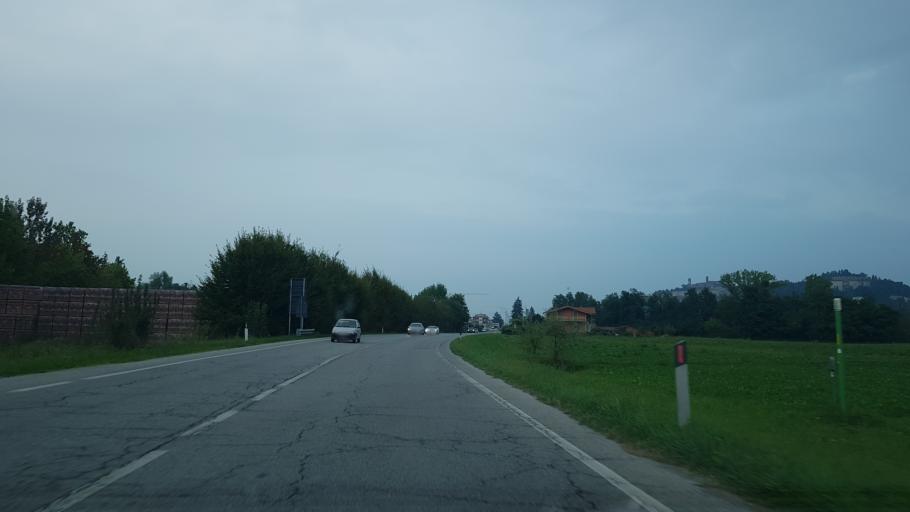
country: IT
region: Piedmont
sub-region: Provincia di Cuneo
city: Mondovi
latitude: 44.3760
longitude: 7.8083
